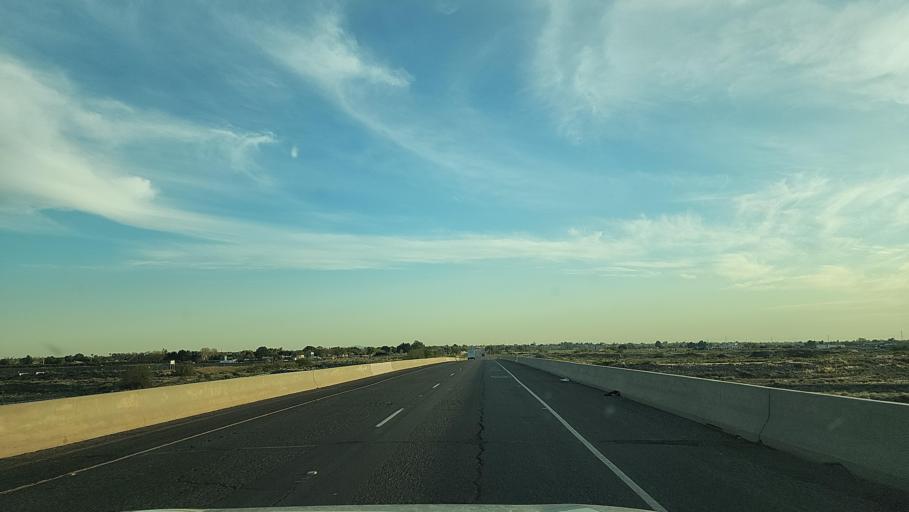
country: US
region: Arizona
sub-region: Maricopa County
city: Mesa
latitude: 33.4866
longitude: -111.7876
